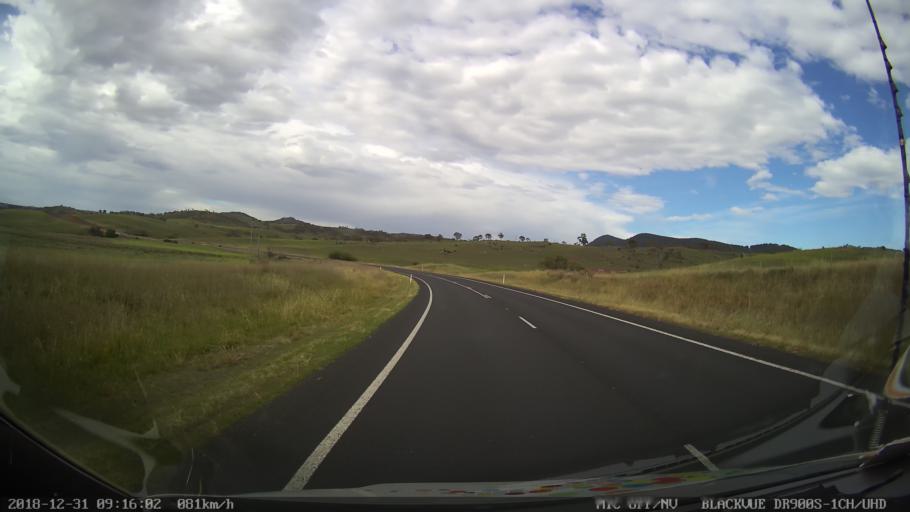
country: AU
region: New South Wales
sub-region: Snowy River
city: Jindabyne
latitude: -36.3916
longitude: 148.5951
